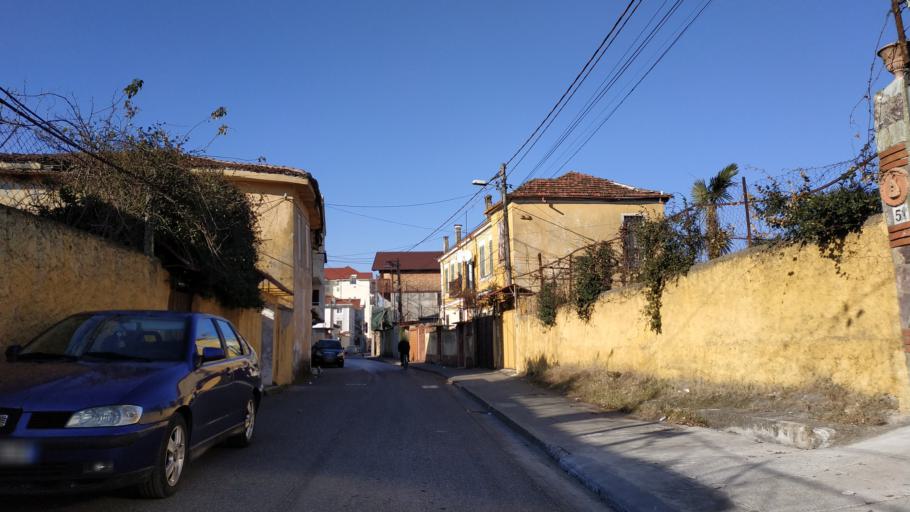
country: AL
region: Shkoder
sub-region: Rrethi i Shkodres
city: Shkoder
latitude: 42.0633
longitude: 19.5203
